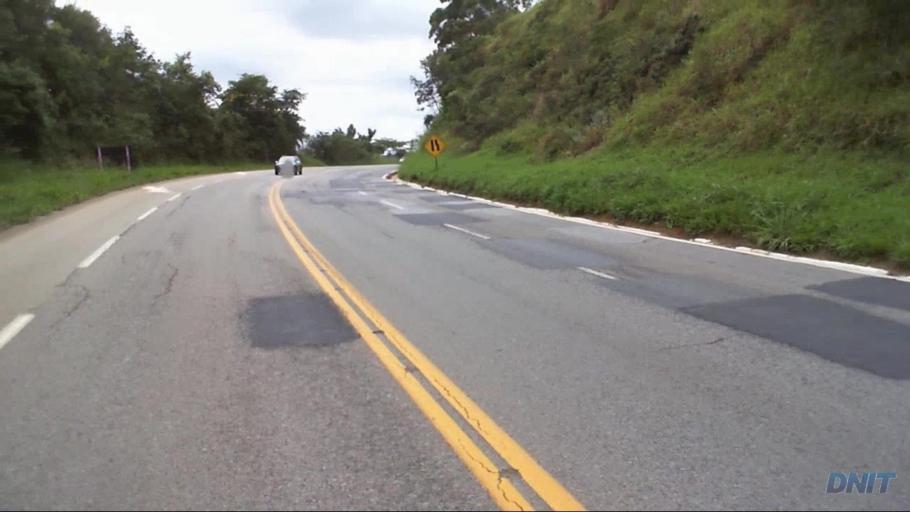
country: BR
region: Minas Gerais
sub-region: Barao De Cocais
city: Barao de Cocais
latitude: -19.8277
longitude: -43.3826
